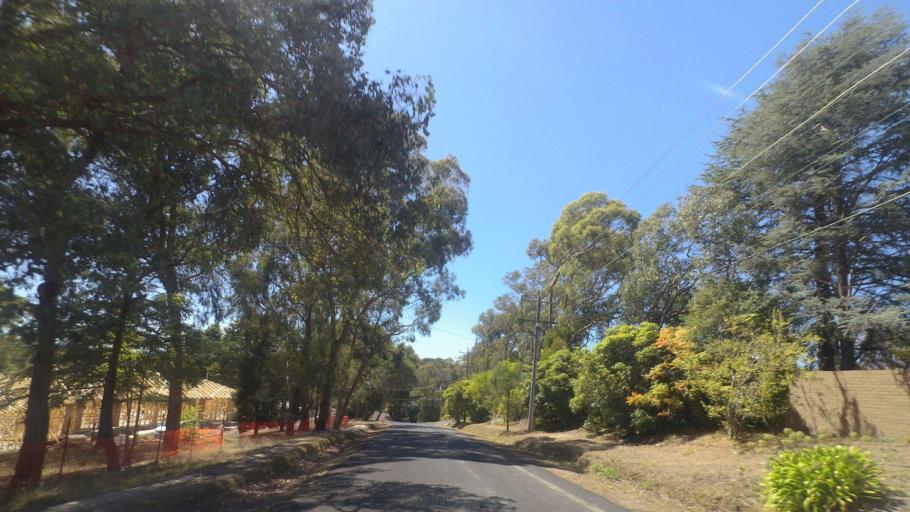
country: AU
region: Victoria
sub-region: Manningham
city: Donvale
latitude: -37.7903
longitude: 145.1897
